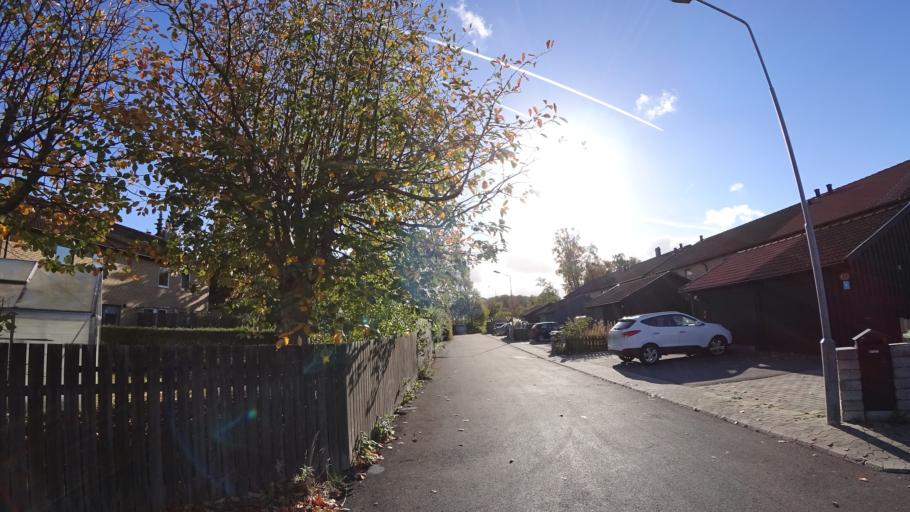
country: SE
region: Skane
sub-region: Staffanstorps Kommun
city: Hjaerup
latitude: 55.6658
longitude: 13.1498
